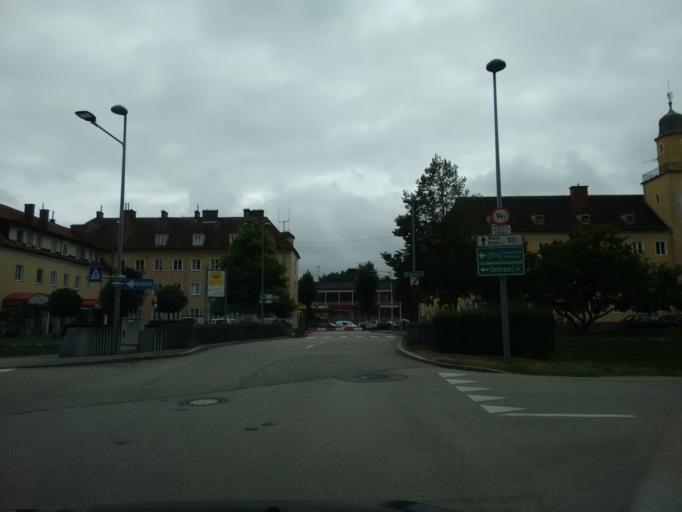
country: AT
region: Upper Austria
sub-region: Politischer Bezirk Grieskirchen
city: Grieskirchen
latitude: 48.2349
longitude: 13.8266
